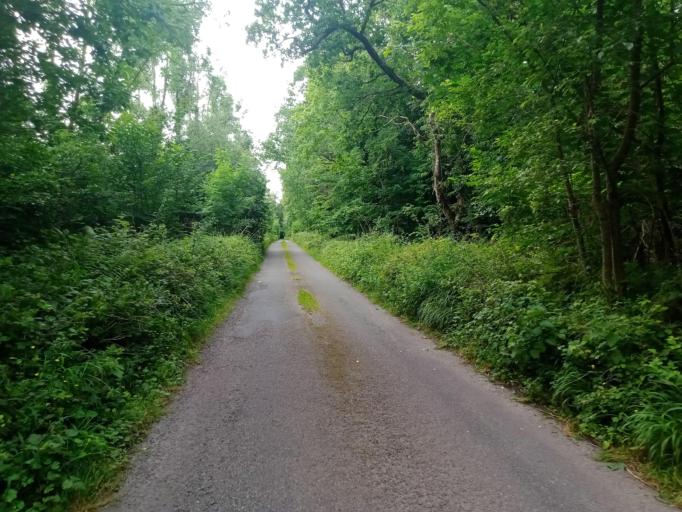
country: IE
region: Leinster
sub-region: Laois
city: Abbeyleix
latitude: 52.9025
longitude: -7.3614
